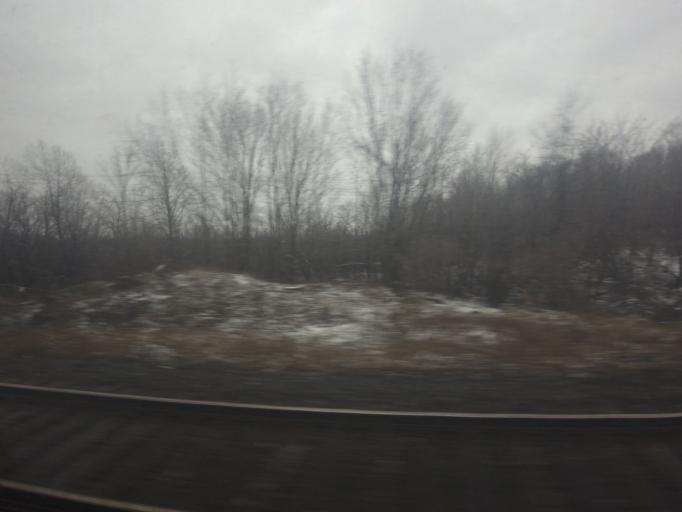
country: CA
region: Ontario
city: Gananoque
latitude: 44.3589
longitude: -76.1975
